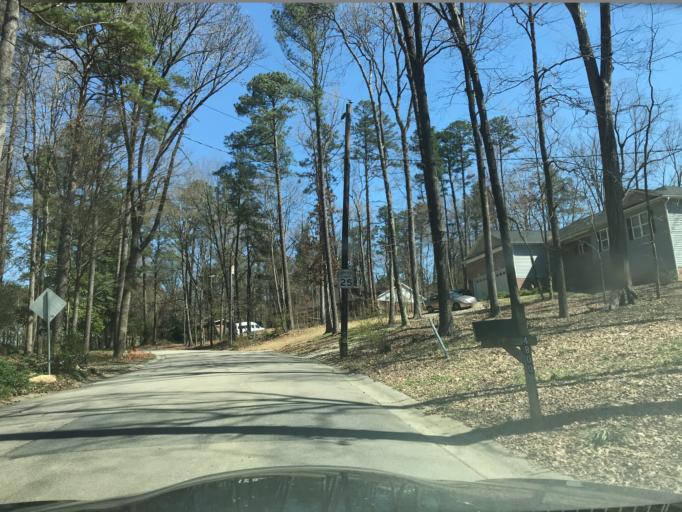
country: US
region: North Carolina
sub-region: Wake County
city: Raleigh
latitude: 35.8450
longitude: -78.5982
